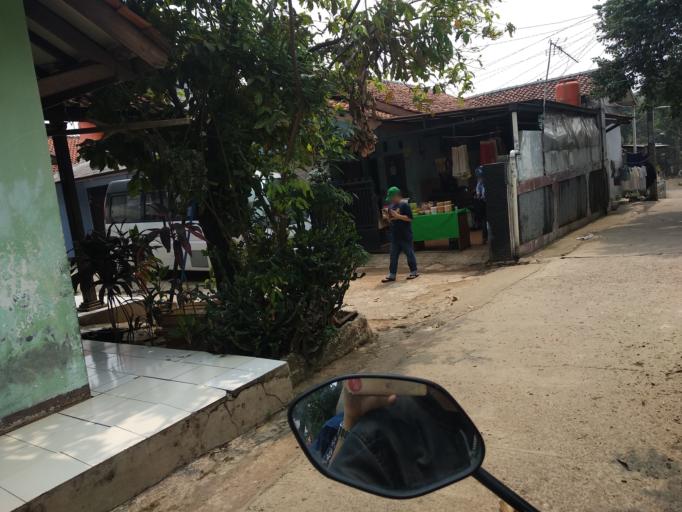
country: ID
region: West Java
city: Depok
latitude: -6.3587
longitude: 106.8398
